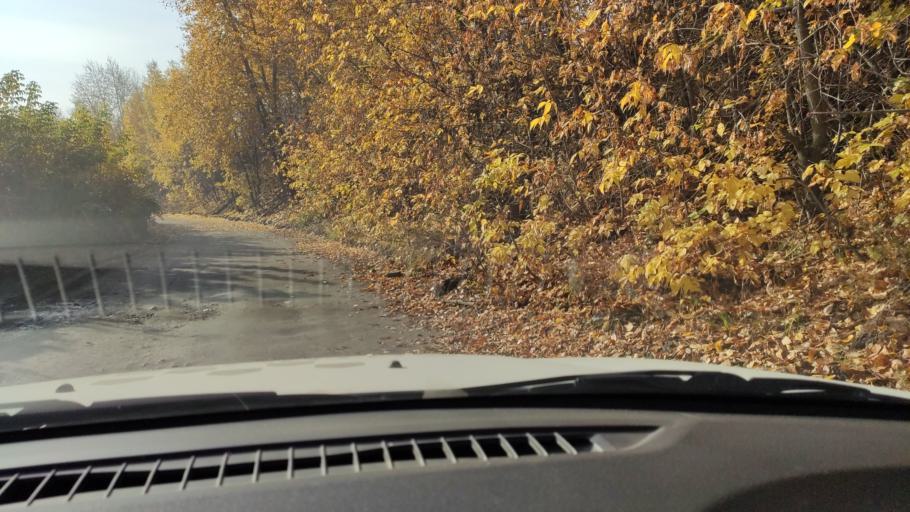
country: RU
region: Perm
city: Kondratovo
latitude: 58.0081
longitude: 56.1574
